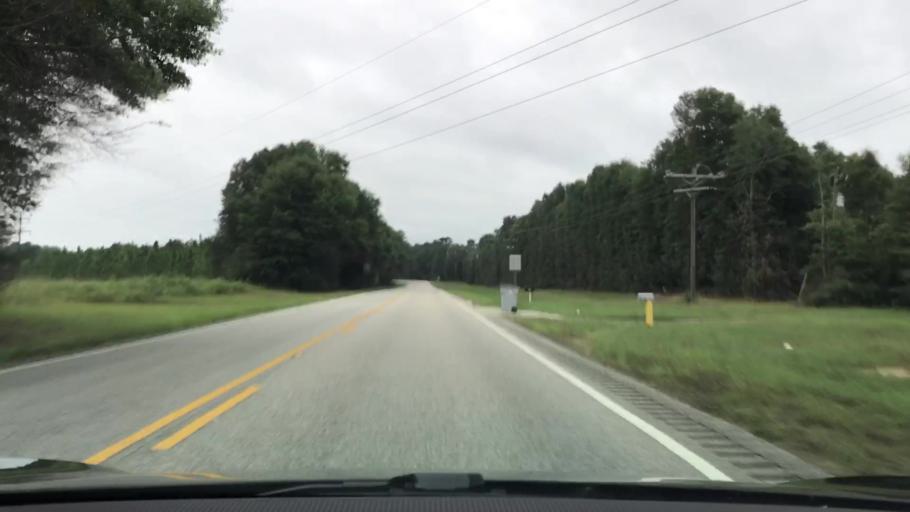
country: US
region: Alabama
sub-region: Coffee County
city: Elba
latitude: 31.3799
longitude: -86.0893
